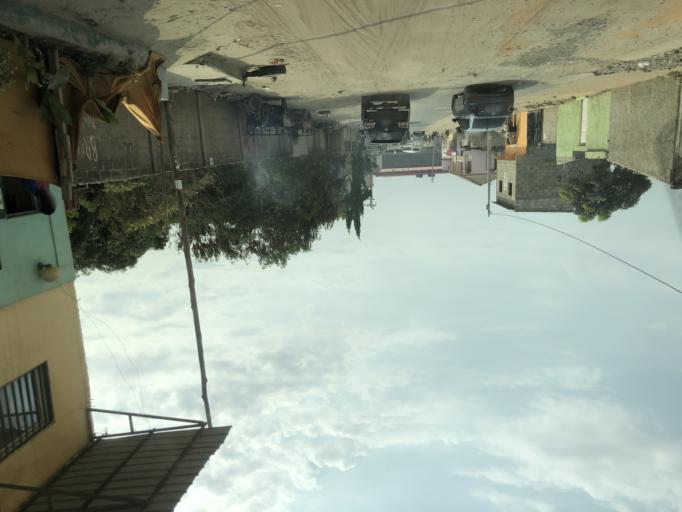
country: AO
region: Luanda
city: Luanda
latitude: -8.9012
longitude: 13.3484
